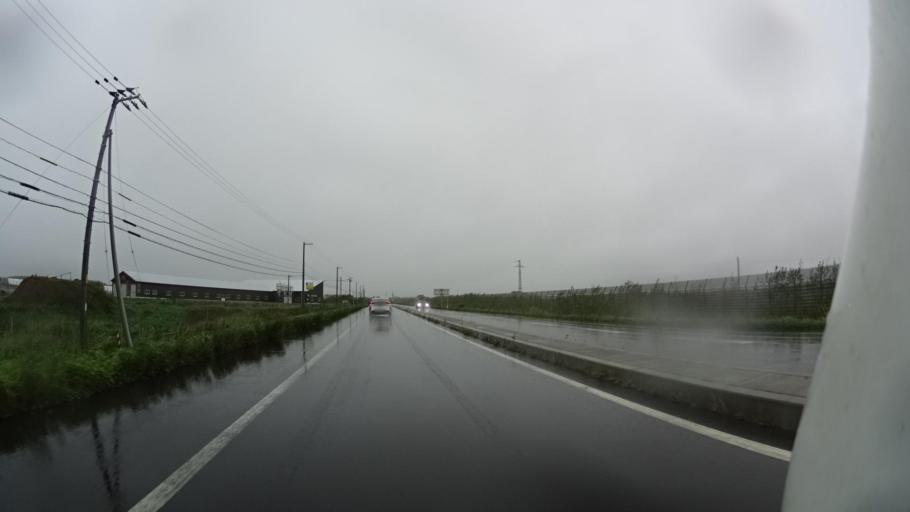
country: JP
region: Hokkaido
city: Nemuro
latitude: 43.2464
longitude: 145.3111
